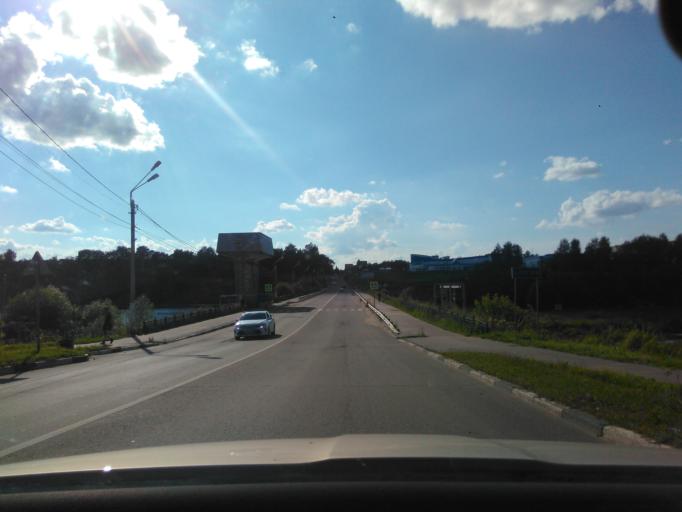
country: RU
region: Moskovskaya
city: Klin
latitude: 56.3178
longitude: 36.7386
